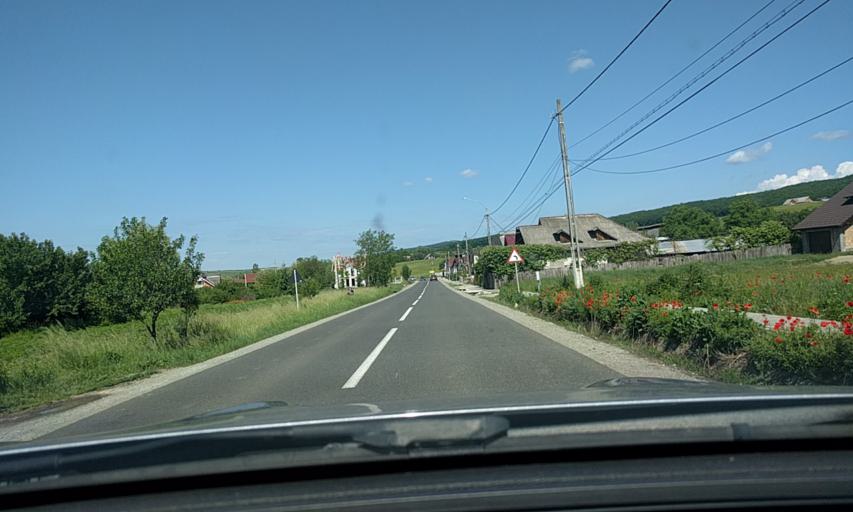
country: RO
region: Bistrita-Nasaud
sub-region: Comuna Dumitra
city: Dumitra
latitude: 47.2309
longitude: 24.4557
